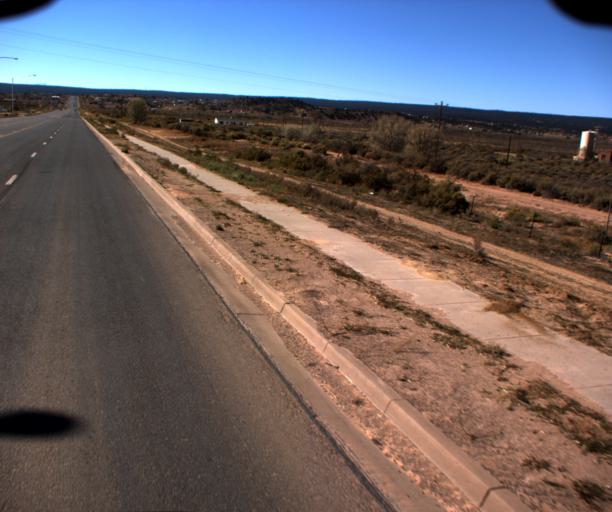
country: US
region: Arizona
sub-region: Apache County
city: Window Rock
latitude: 35.6608
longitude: -109.0713
